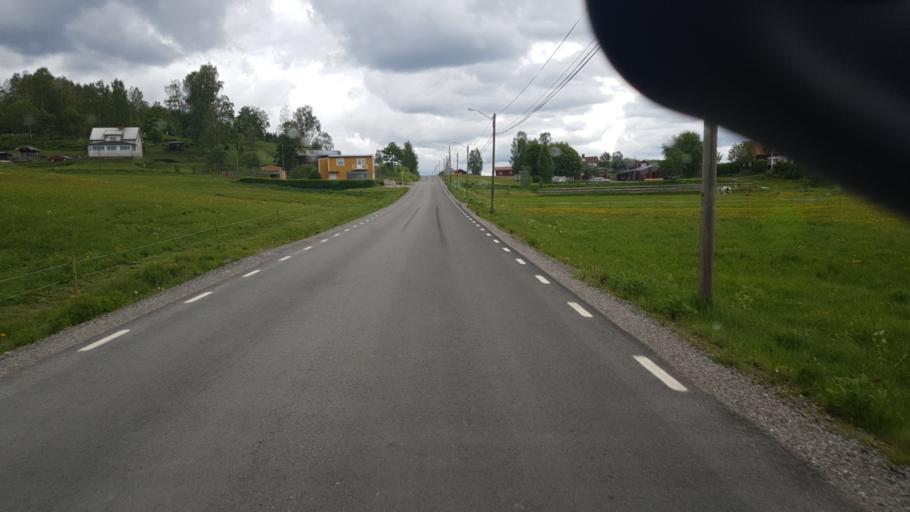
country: SE
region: Vaermland
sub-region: Eda Kommun
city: Charlottenberg
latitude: 59.9340
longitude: 12.5222
